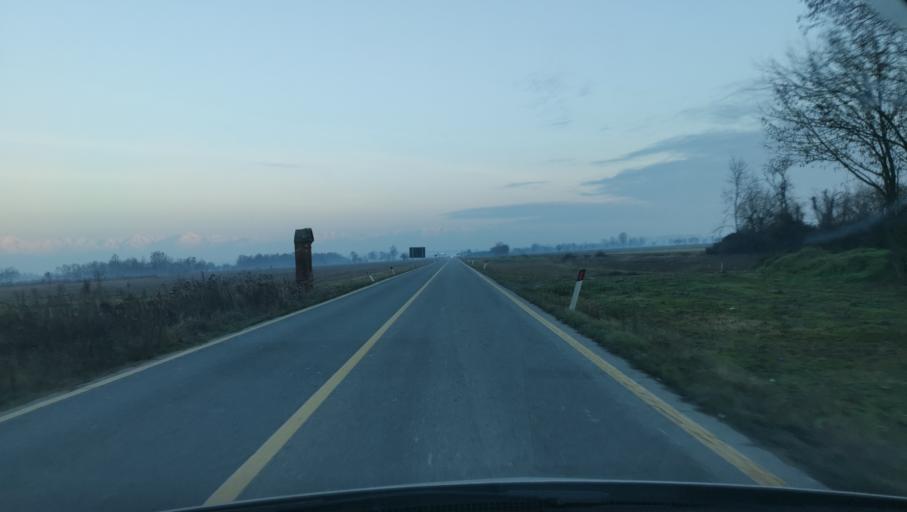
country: IT
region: Piedmont
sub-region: Provincia di Torino
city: Montanaro
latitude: 45.2304
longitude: 7.8909
